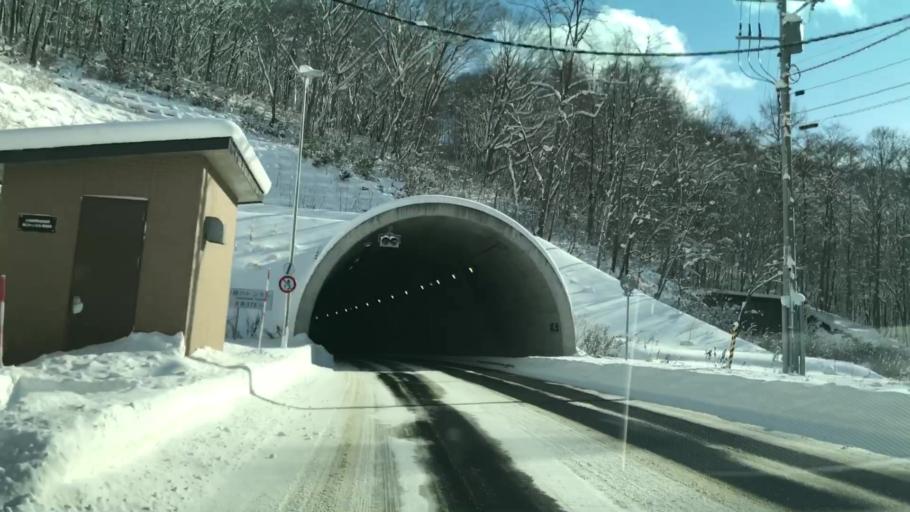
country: JP
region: Hokkaido
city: Yoichi
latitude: 43.2218
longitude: 140.7368
